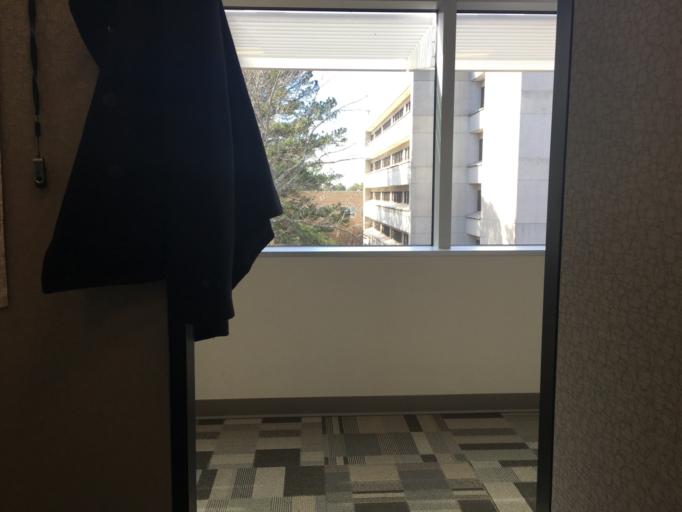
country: US
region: North Carolina
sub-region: Wake County
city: Morrisville
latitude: 35.9053
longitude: -78.8653
